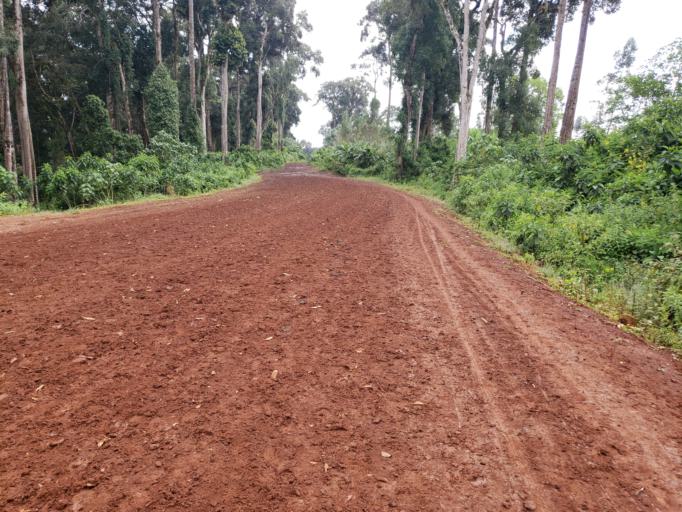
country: ET
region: Oromiya
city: Dodola
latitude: 6.5630
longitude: 39.4247
